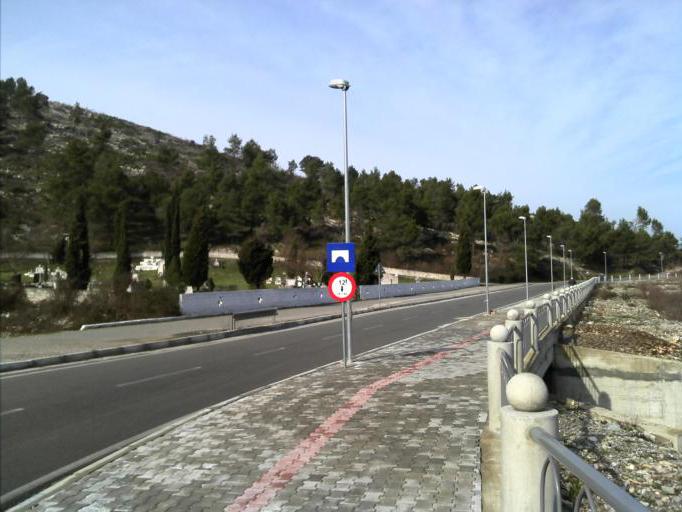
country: AL
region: Shkoder
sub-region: Rrethi i Shkodres
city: Berdica e Madhe
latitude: 42.0554
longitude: 19.4686
